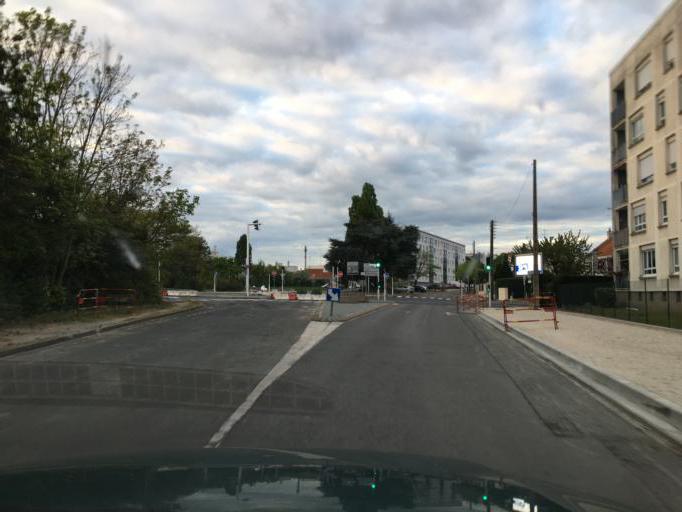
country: FR
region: Centre
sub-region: Departement du Loiret
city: Saint-Jean-de-la-Ruelle
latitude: 47.9056
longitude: 1.8715
